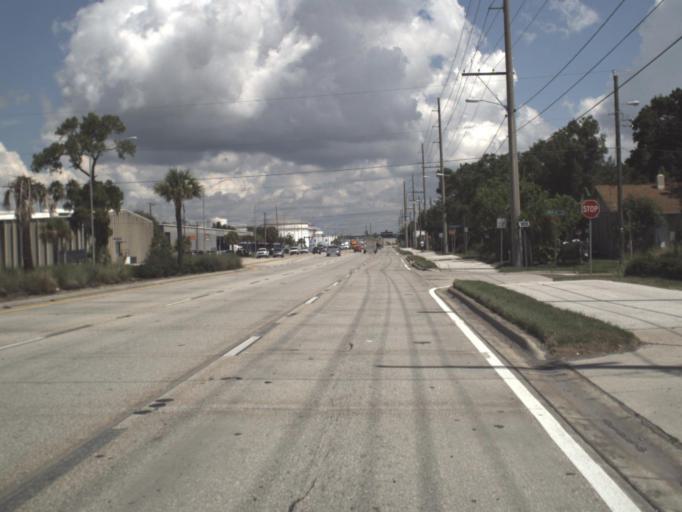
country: US
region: Florida
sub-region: Hillsborough County
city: Tampa
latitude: 27.9399
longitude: -82.4365
